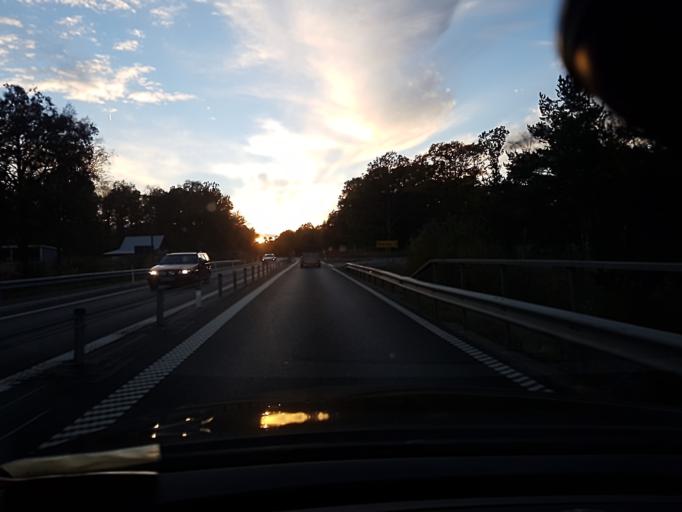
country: SE
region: Kronoberg
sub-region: Ljungby Kommun
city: Ljungby
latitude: 56.7607
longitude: 13.7760
